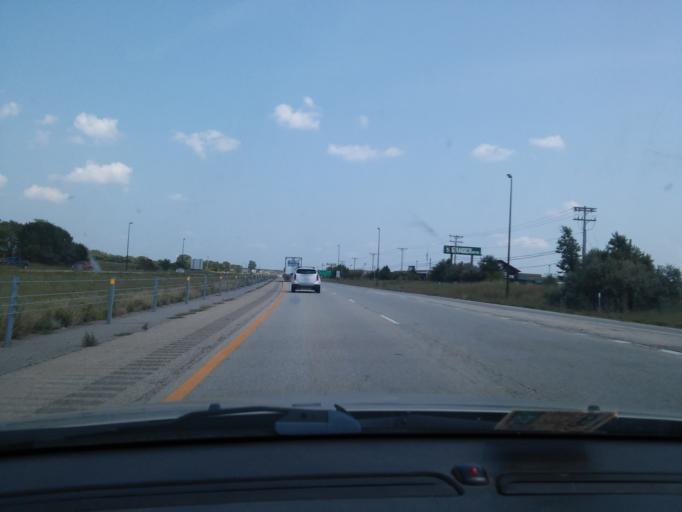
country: US
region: Illinois
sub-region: Sangamon County
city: Jerome
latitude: 39.7417
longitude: -89.7015
